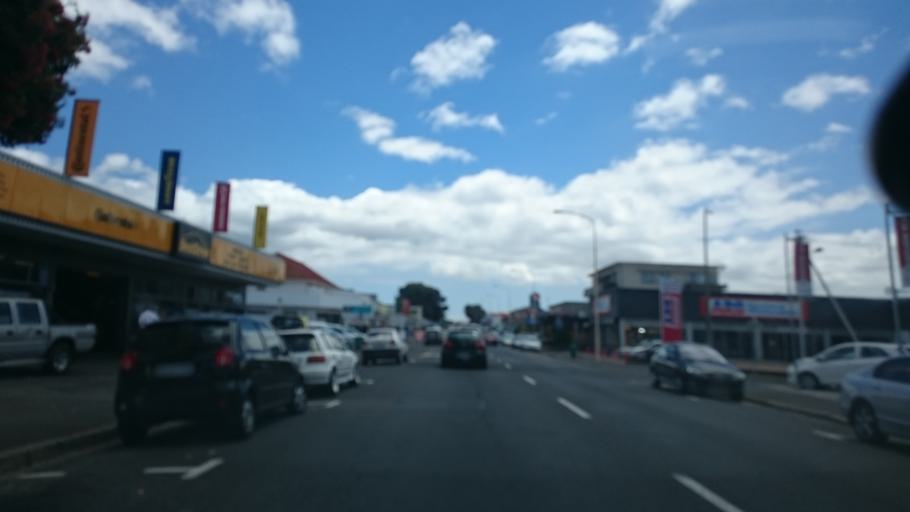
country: ZA
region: Western Cape
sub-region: City of Cape Town
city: Bergvliet
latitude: -34.0385
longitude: 18.4645
